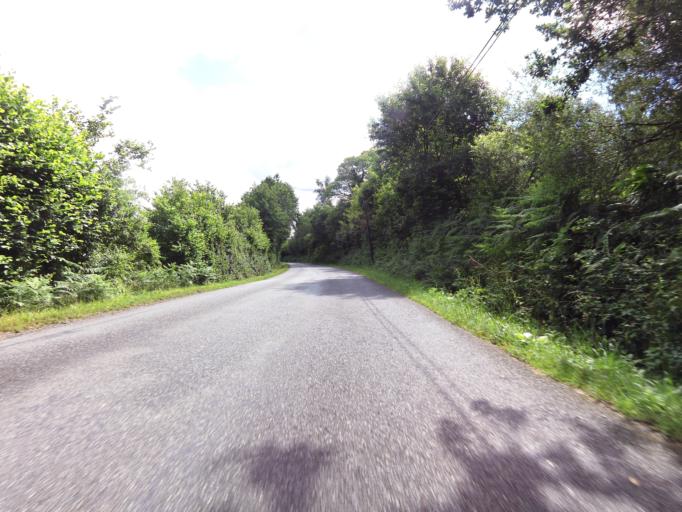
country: FR
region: Brittany
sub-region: Departement du Morbihan
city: Malansac
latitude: 47.7034
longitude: -2.2860
